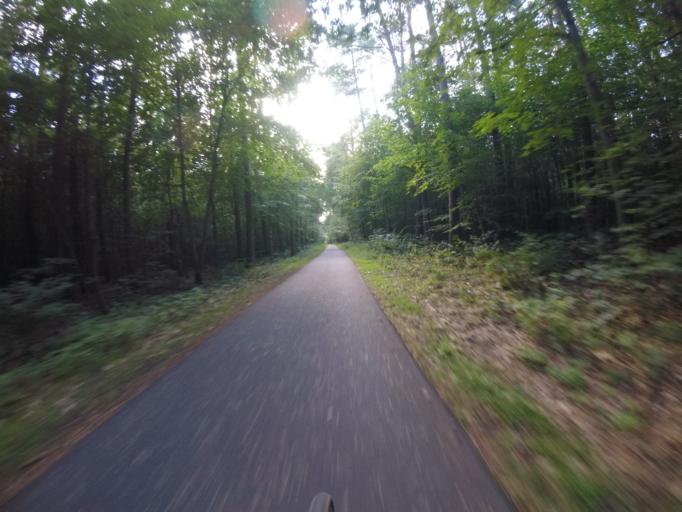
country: DE
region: Brandenburg
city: Petershagen
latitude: 52.5536
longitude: 13.7929
